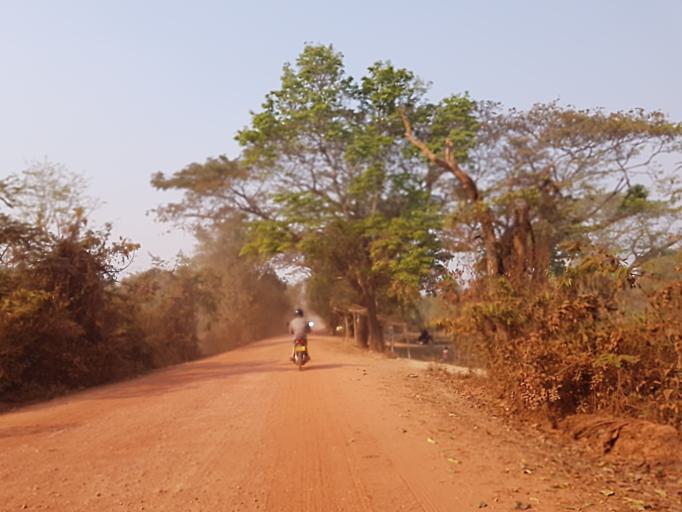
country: TH
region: Nong Khai
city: Phon Phisai
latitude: 18.0058
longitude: 102.9082
